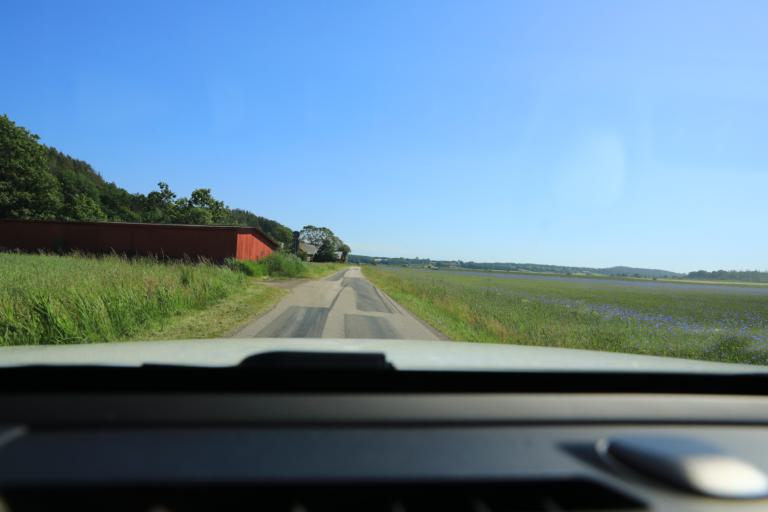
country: SE
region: Halland
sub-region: Varbergs Kommun
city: Veddige
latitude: 57.1809
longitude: 12.3159
